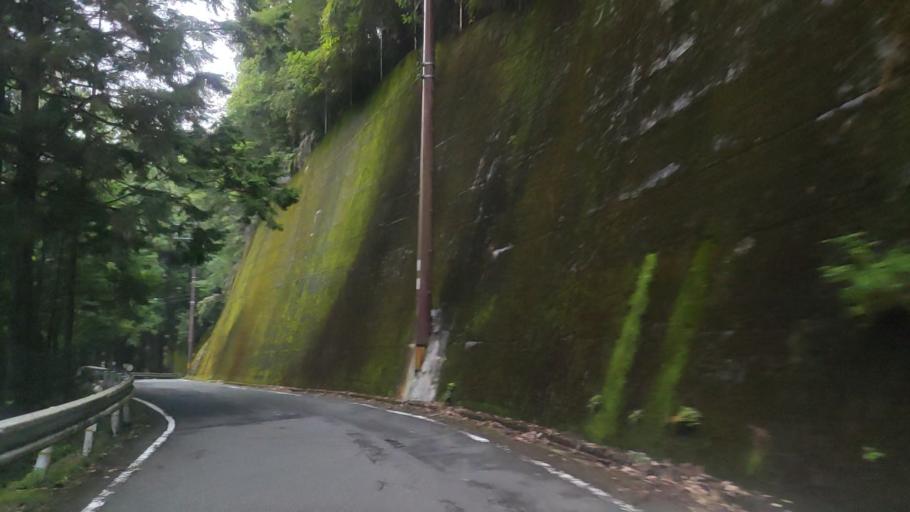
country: JP
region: Wakayama
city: Koya
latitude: 34.2397
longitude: 135.6522
